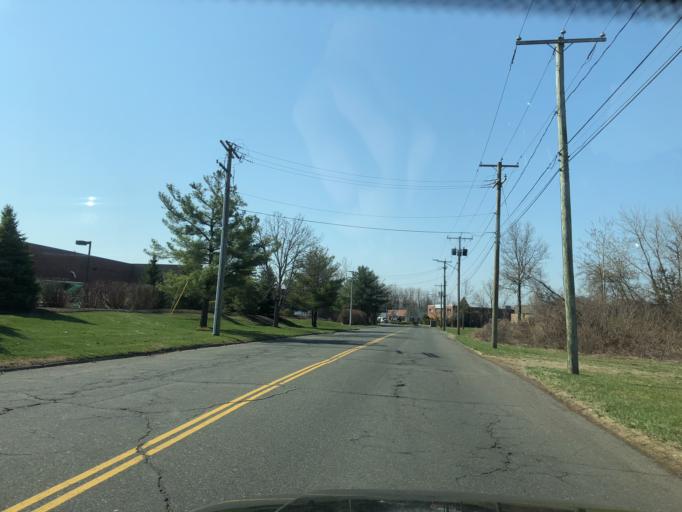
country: US
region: Connecticut
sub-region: Hartford County
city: Newington
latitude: 41.6696
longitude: -72.7220
